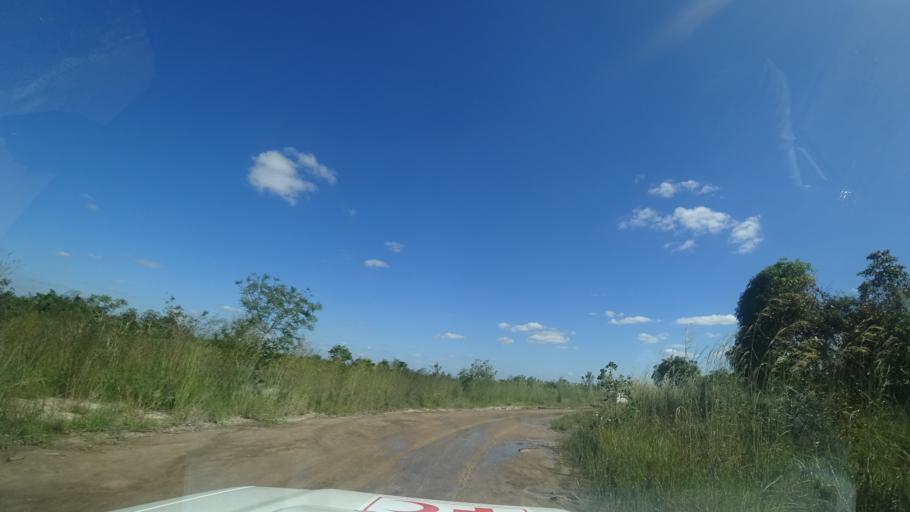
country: MZ
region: Sofala
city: Dondo
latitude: -19.4760
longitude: 34.6297
